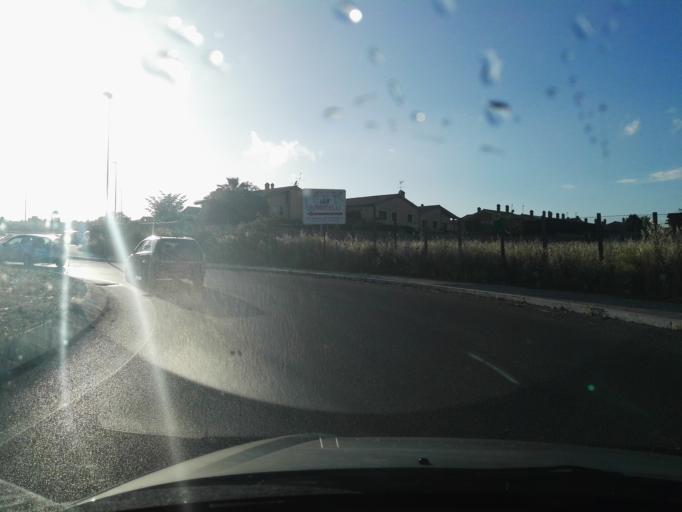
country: IT
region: Latium
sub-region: Citta metropolitana di Roma Capitale
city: Selcetta
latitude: 41.7855
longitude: 12.4792
